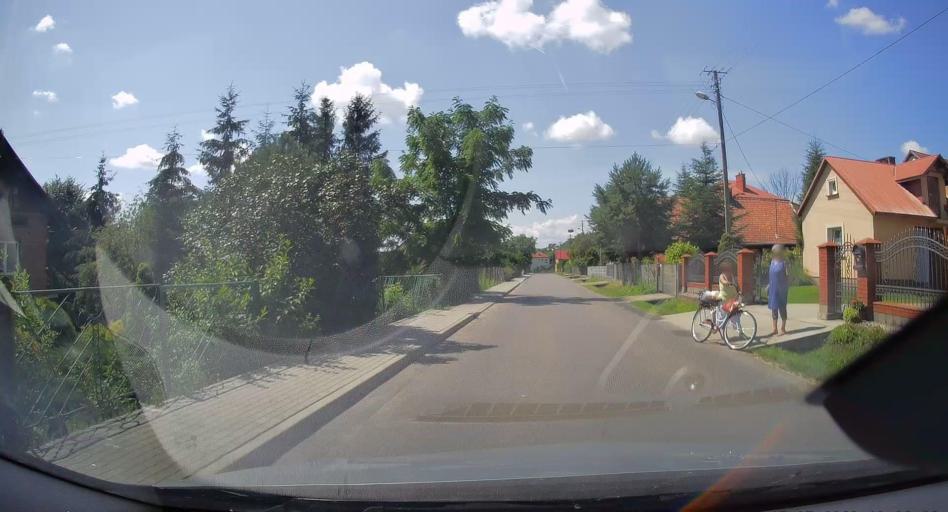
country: PL
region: Subcarpathian Voivodeship
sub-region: Powiat przemyski
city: Medyka
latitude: 49.8257
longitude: 22.8682
